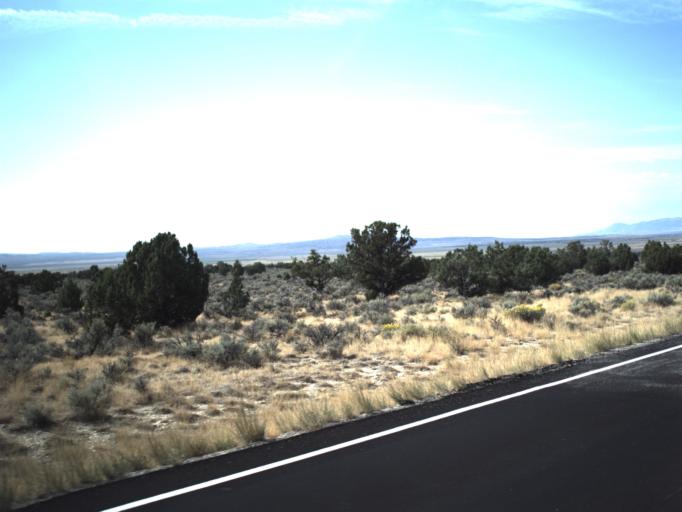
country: US
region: Idaho
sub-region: Cassia County
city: Burley
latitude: 41.8077
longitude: -113.4472
